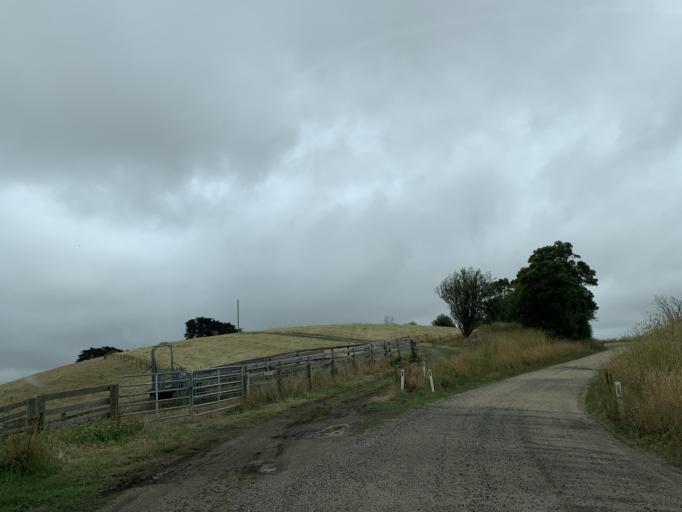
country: AU
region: Victoria
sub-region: Baw Baw
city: Warragul
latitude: -38.3505
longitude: 145.8710
